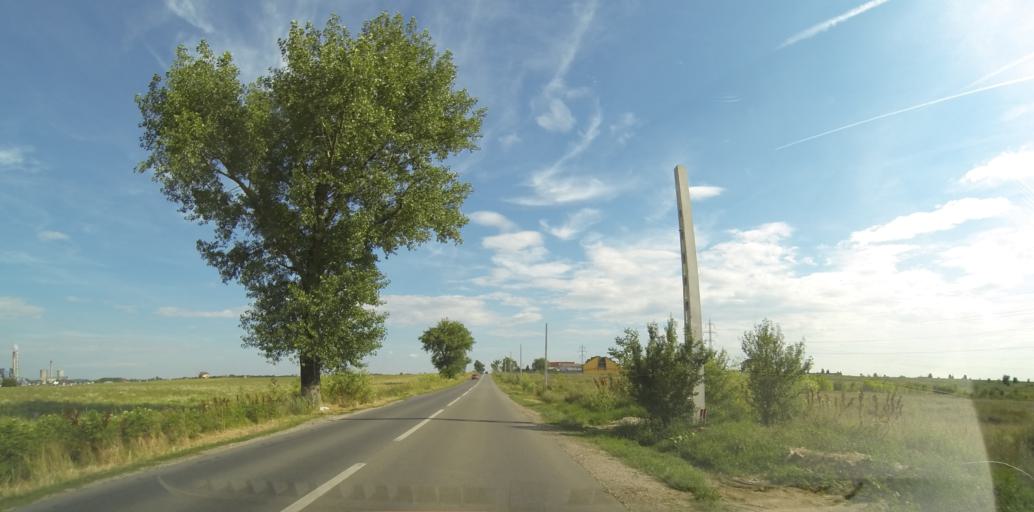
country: RO
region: Dolj
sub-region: Comuna Simnicu de Sus
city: Simnicu de Sus
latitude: 44.3539
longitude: 23.7861
